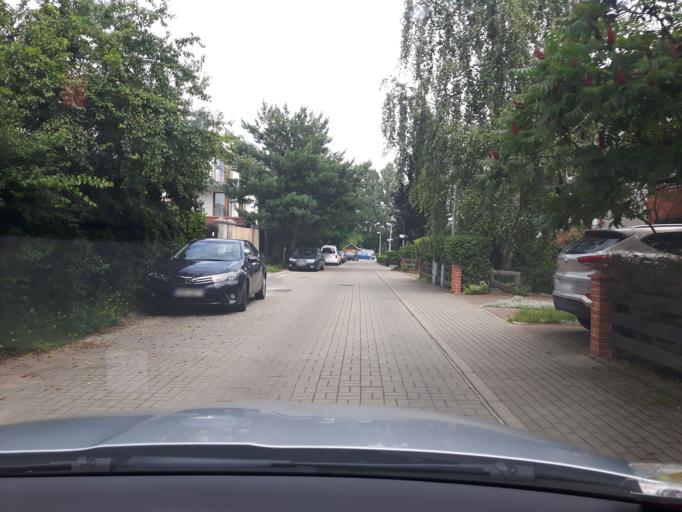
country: PL
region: Pomeranian Voivodeship
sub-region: Sopot
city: Sopot
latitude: 54.4311
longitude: 18.5747
